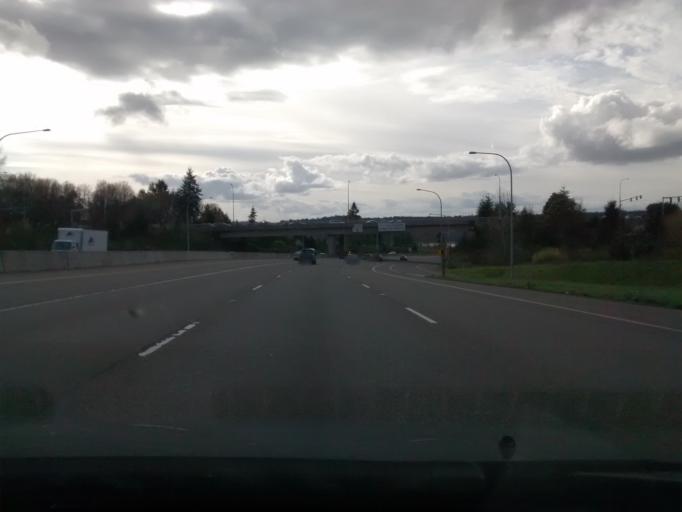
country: US
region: Washington
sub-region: Pierce County
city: Fircrest
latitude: 47.2588
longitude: -122.5347
